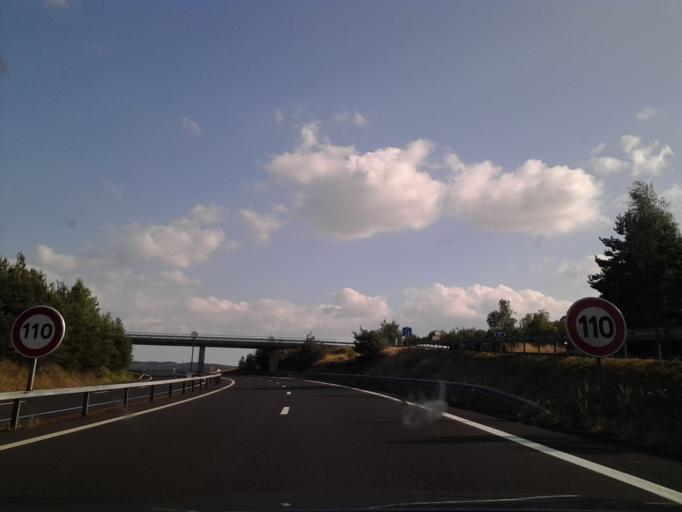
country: FR
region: Auvergne
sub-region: Departement du Cantal
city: Massiac
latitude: 45.1464
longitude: 3.1428
